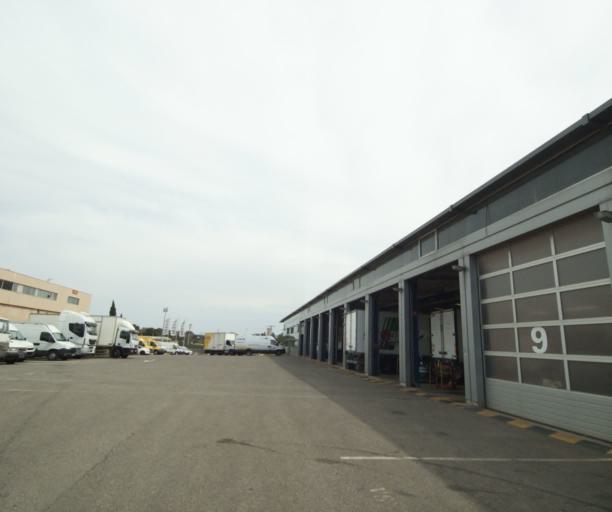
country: FR
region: Provence-Alpes-Cote d'Azur
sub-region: Departement du Var
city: La Farlede
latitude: 43.1496
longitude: 6.0364
